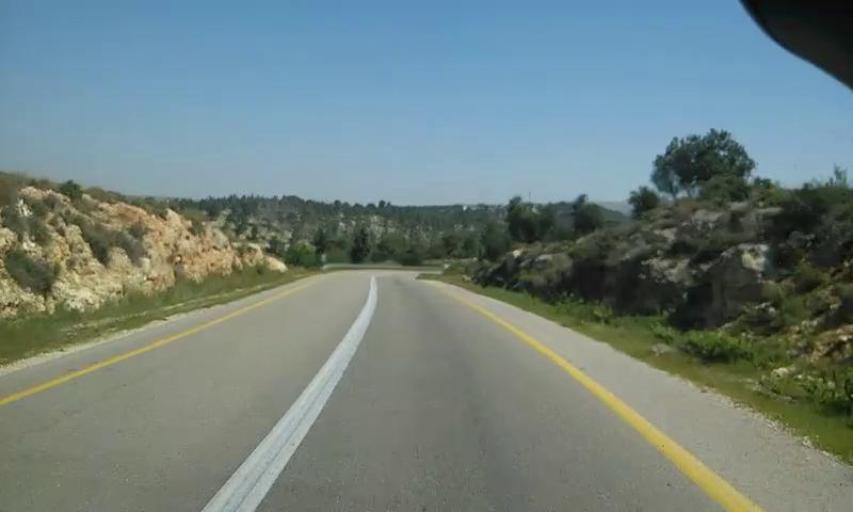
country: PS
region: West Bank
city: Nahhalin
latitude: 31.6739
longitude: 35.0898
